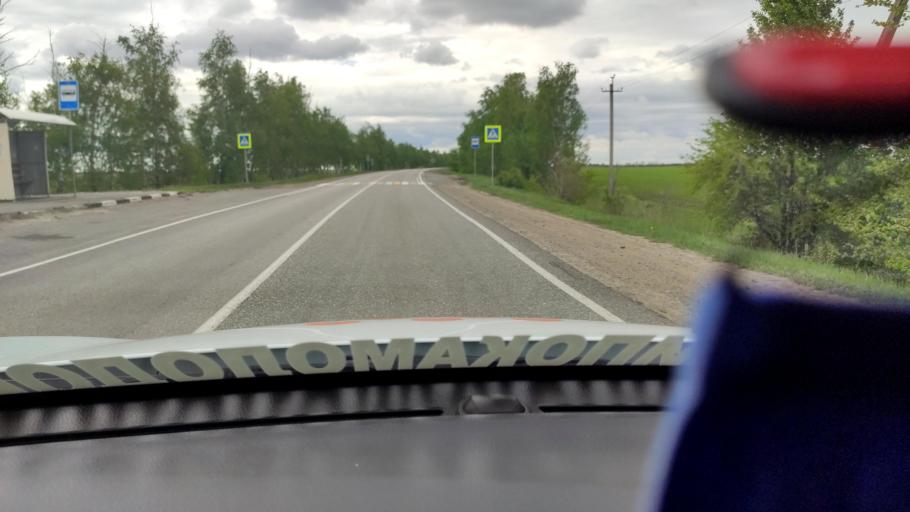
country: RU
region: Voronezj
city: Imeni Pervogo Maya
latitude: 50.7828
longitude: 39.3813
